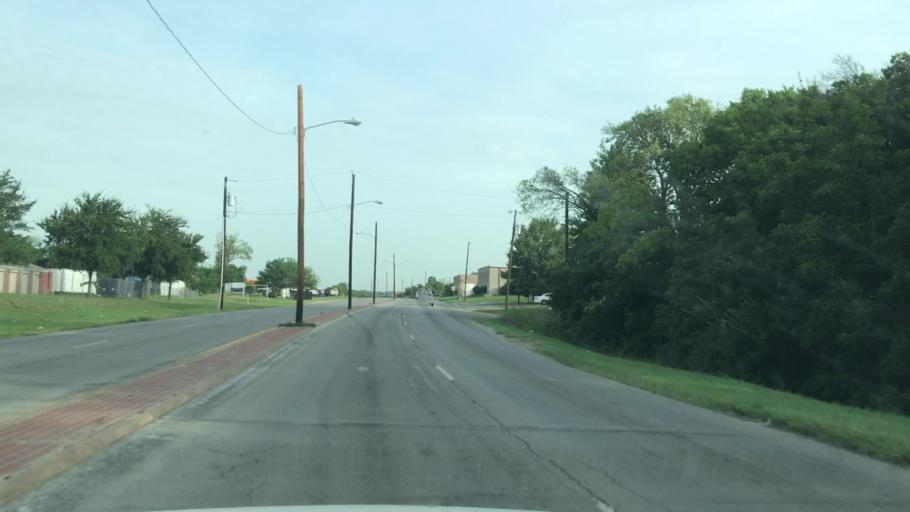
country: US
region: Texas
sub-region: Dallas County
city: Dallas
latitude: 32.7796
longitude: -96.7221
